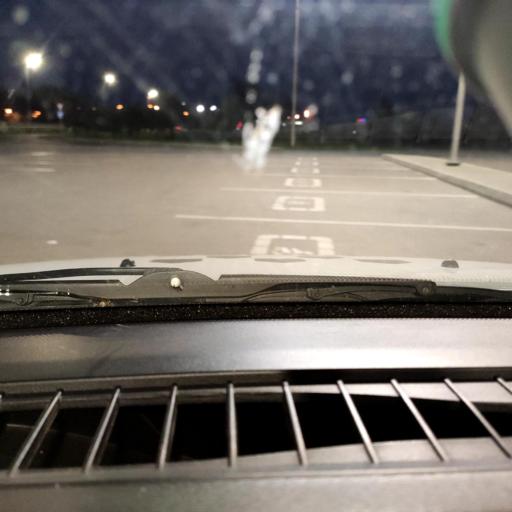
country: RU
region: Tatarstan
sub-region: Tukayevskiy Rayon
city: Naberezhnyye Chelny
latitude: 55.6720
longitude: 52.2781
